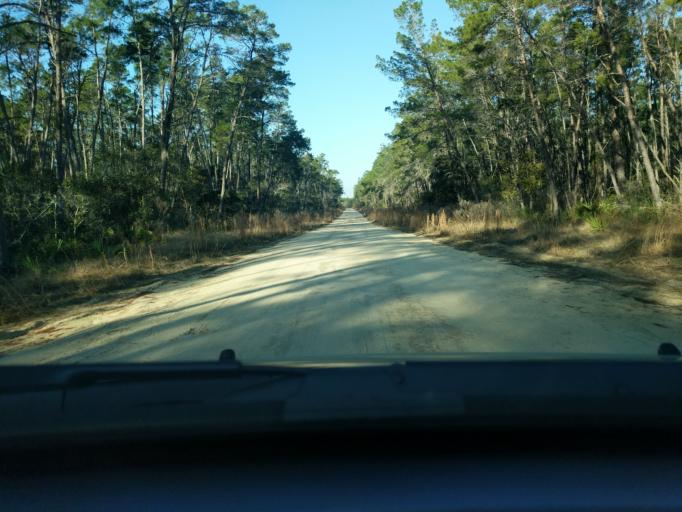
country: US
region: Florida
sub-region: Marion County
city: Silver Springs Shores
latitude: 29.2264
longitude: -81.8223
